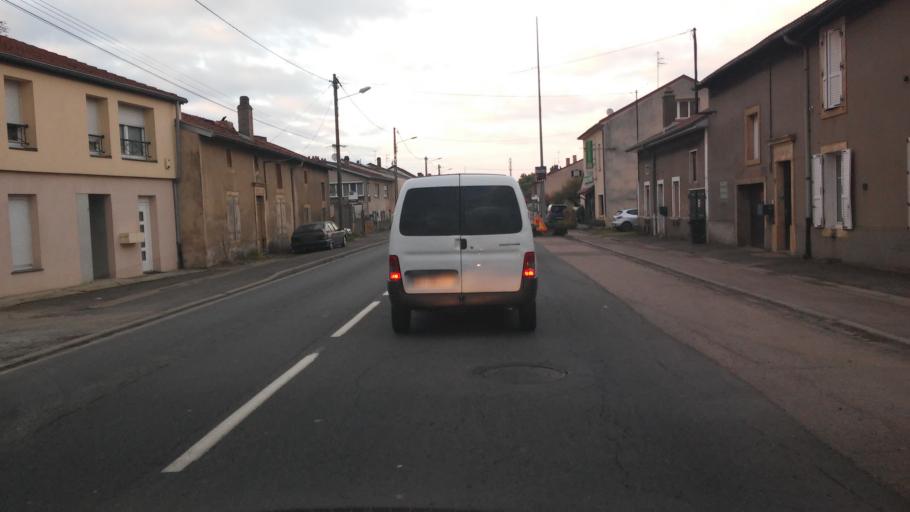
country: FR
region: Lorraine
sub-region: Departement de la Moselle
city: Woippy
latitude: 49.1735
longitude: 6.1623
